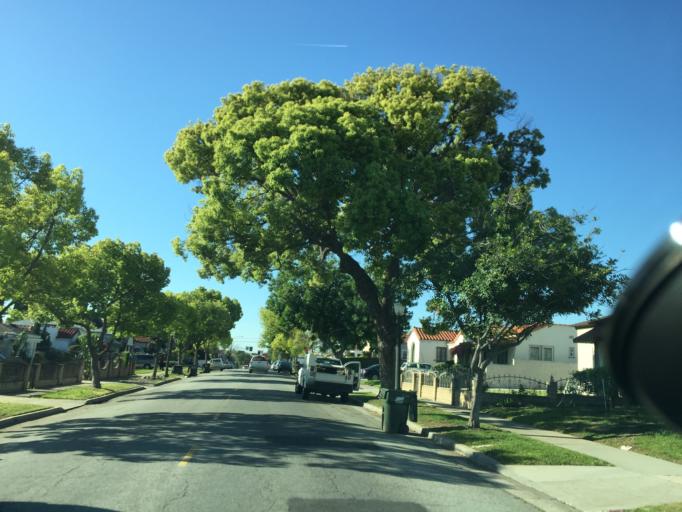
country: US
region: California
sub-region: Los Angeles County
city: Alhambra
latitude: 34.0806
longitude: -118.1199
